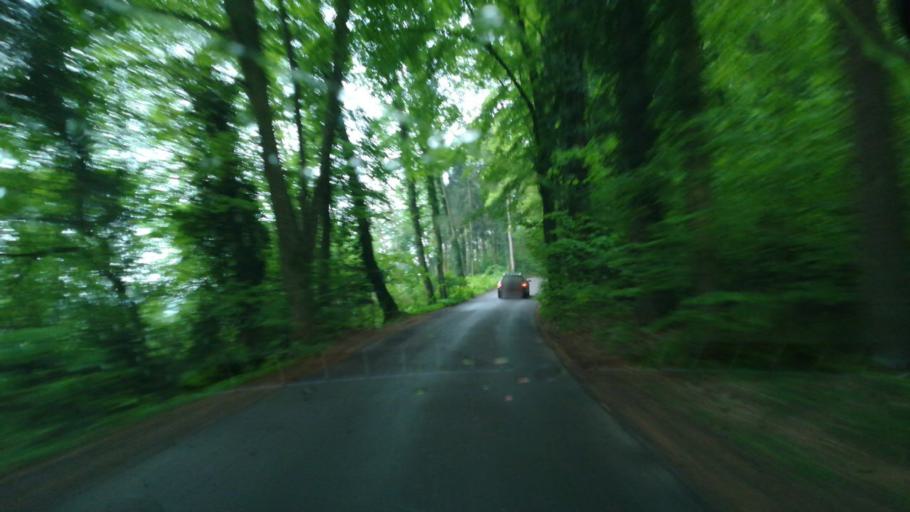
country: CH
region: Zurich
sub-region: Bezirk Buelach
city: Hochfelden
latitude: 47.5203
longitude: 8.4967
